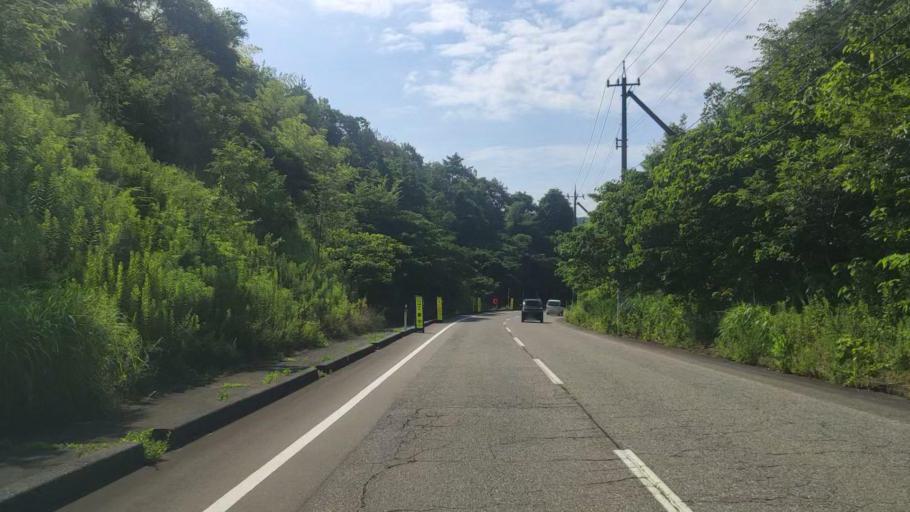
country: JP
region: Ishikawa
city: Komatsu
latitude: 36.3833
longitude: 136.4969
